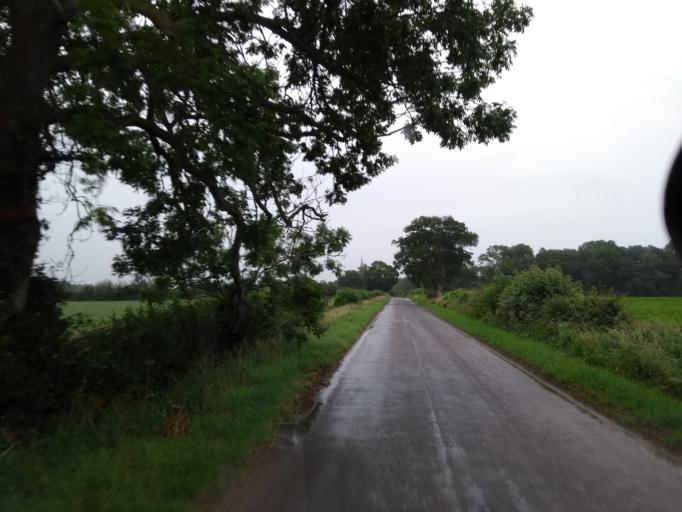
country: GB
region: England
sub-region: Somerset
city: Street
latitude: 51.0837
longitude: -2.6830
